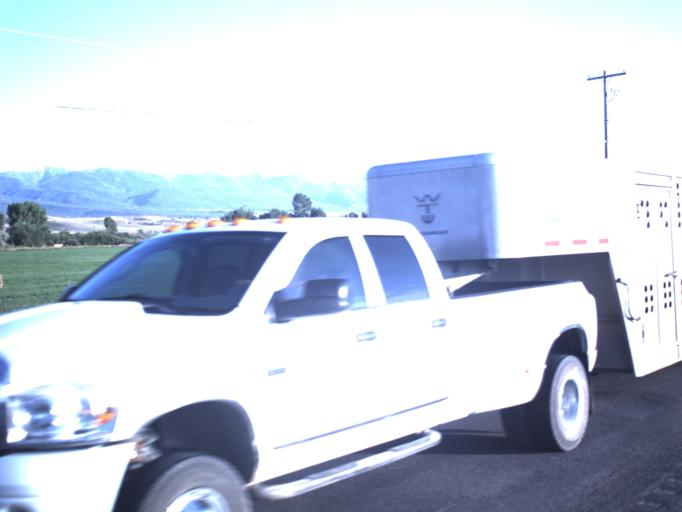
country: US
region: Utah
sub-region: Sanpete County
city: Fairview
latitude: 39.5918
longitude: -111.4481
